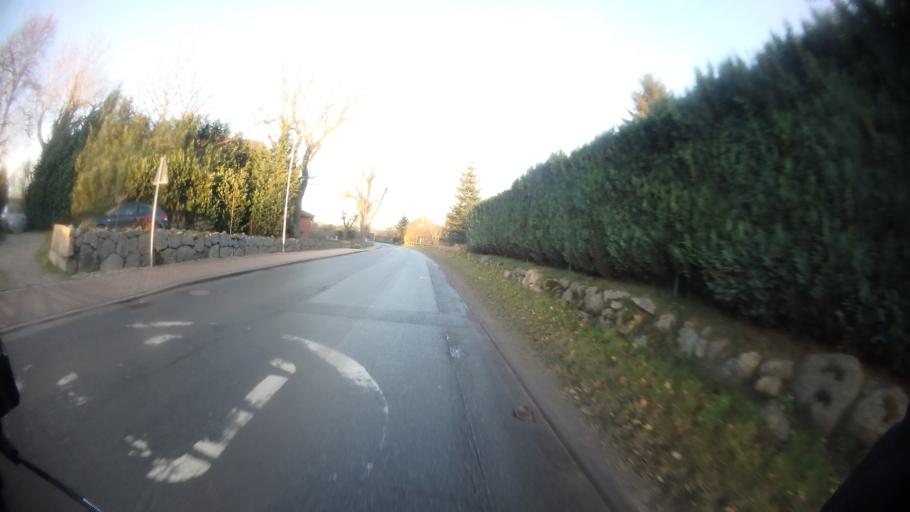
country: DE
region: Schleswig-Holstein
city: Scharbeutz
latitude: 54.0117
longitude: 10.7003
